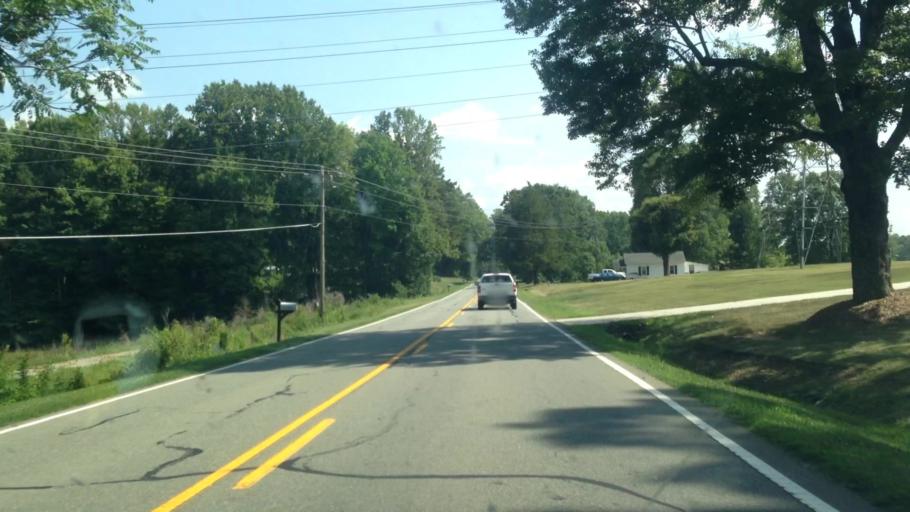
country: US
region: North Carolina
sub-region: Stokes County
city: Walnut Cove
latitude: 36.2743
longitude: -80.0883
